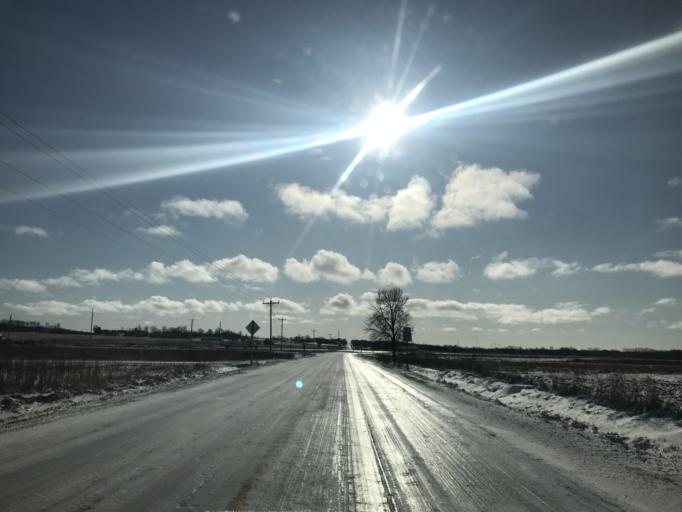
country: US
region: Wisconsin
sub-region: Kewaunee County
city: Luxemburg
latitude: 44.7210
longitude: -87.6208
